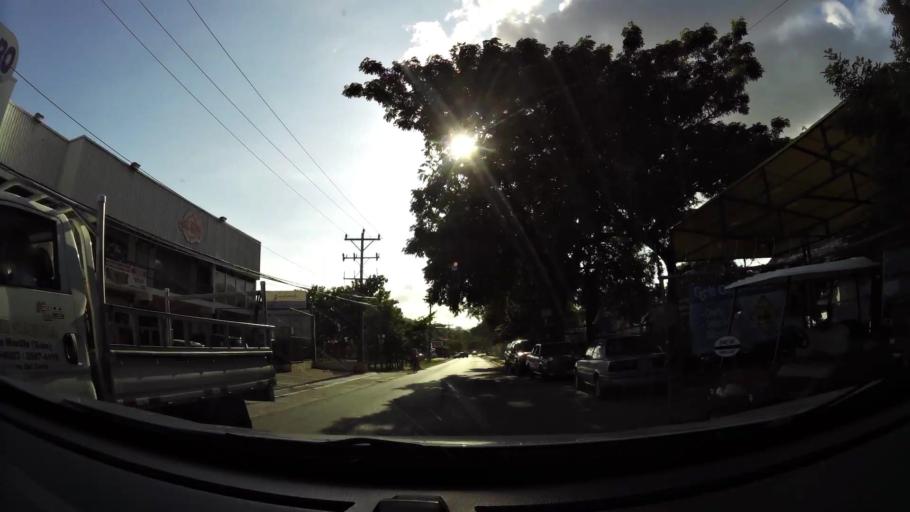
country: CR
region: Guanacaste
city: Sardinal
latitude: 10.5487
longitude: -85.6963
